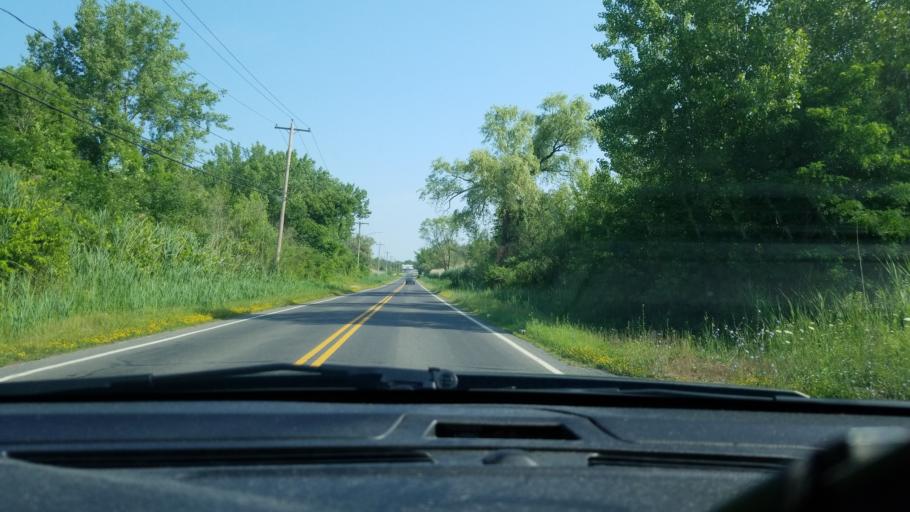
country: US
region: New York
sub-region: Onondaga County
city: East Syracuse
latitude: 43.1139
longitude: -76.0733
